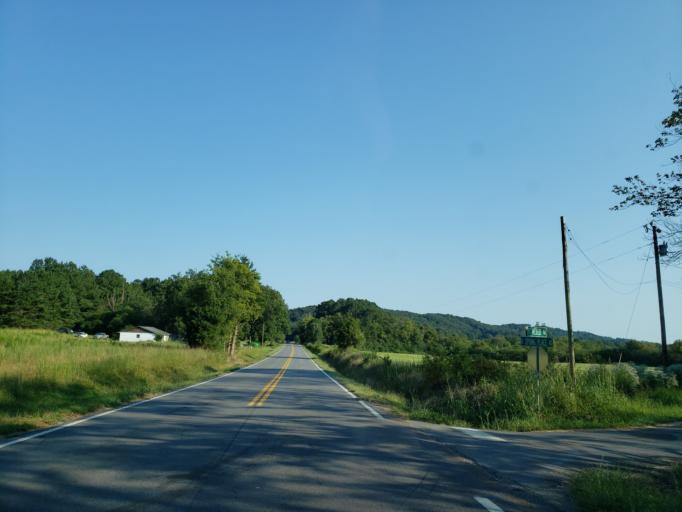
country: US
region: Tennessee
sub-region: Bradley County
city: Wildwood Lake
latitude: 35.0112
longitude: -84.7898
